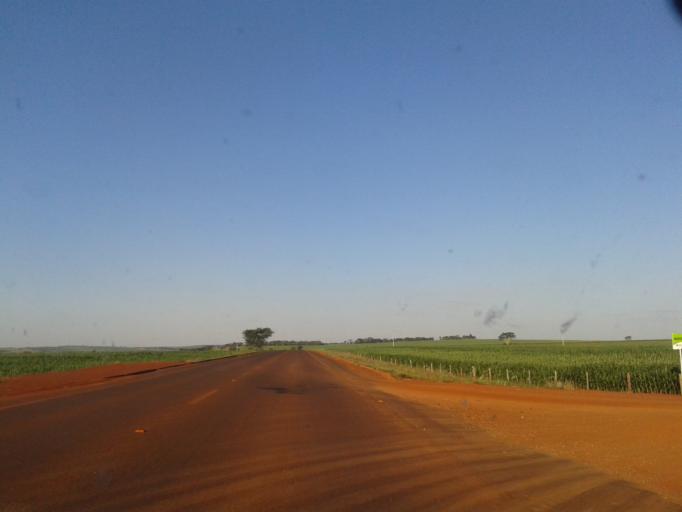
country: BR
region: Minas Gerais
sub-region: Capinopolis
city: Capinopolis
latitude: -18.6987
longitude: -49.6429
